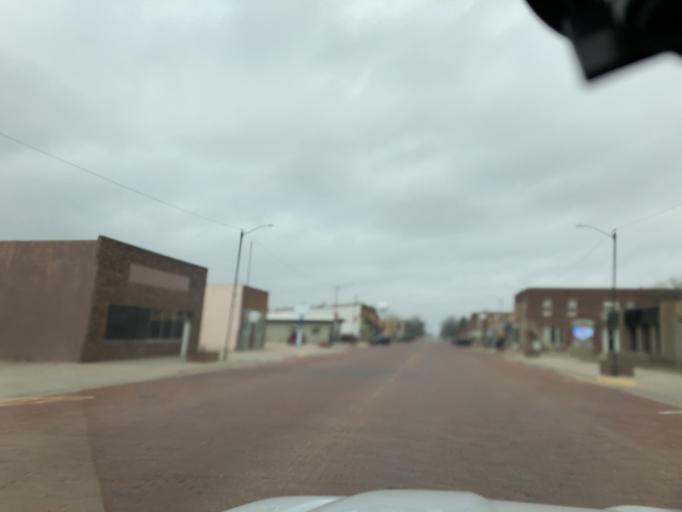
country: US
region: Kansas
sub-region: Stafford County
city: Stafford
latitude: 37.9599
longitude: -98.6004
